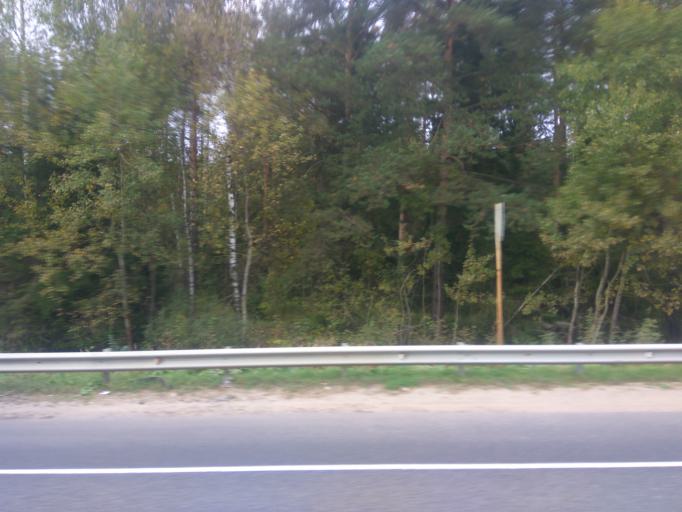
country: RU
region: Moskovskaya
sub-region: Shchelkovskiy Rayon
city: Grebnevo
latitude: 56.0020
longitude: 38.1294
